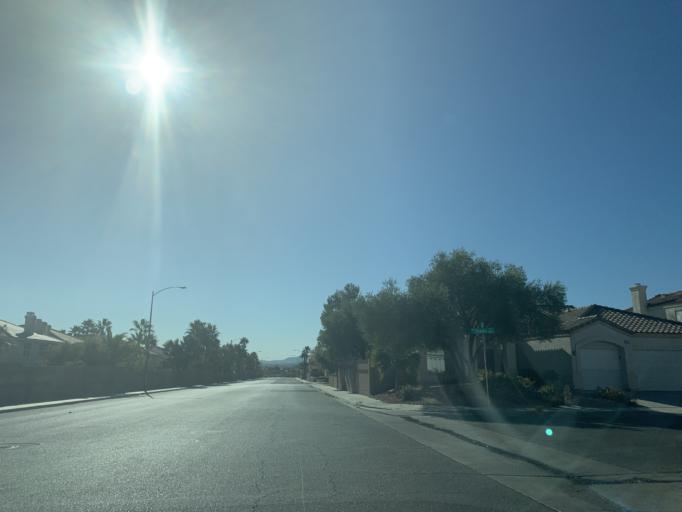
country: US
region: Nevada
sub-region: Clark County
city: Spring Valley
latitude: 36.1213
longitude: -115.2835
